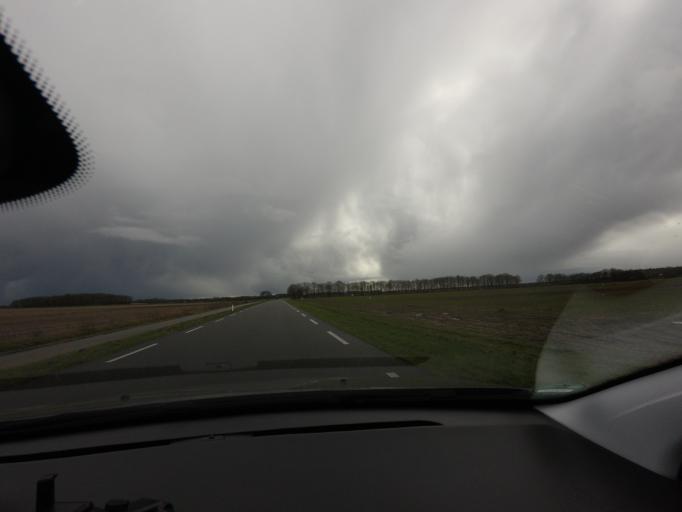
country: NL
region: Drenthe
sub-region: Gemeente Borger-Odoorn
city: Borger
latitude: 52.9423
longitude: 6.7887
